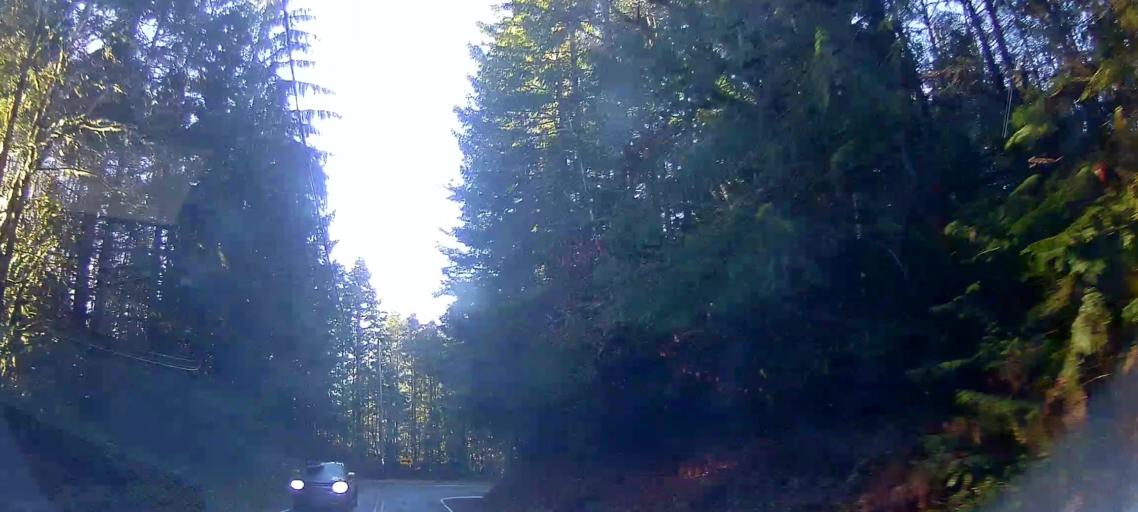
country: US
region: Washington
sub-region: Snohomish County
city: Darrington
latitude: 48.5731
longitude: -121.7736
